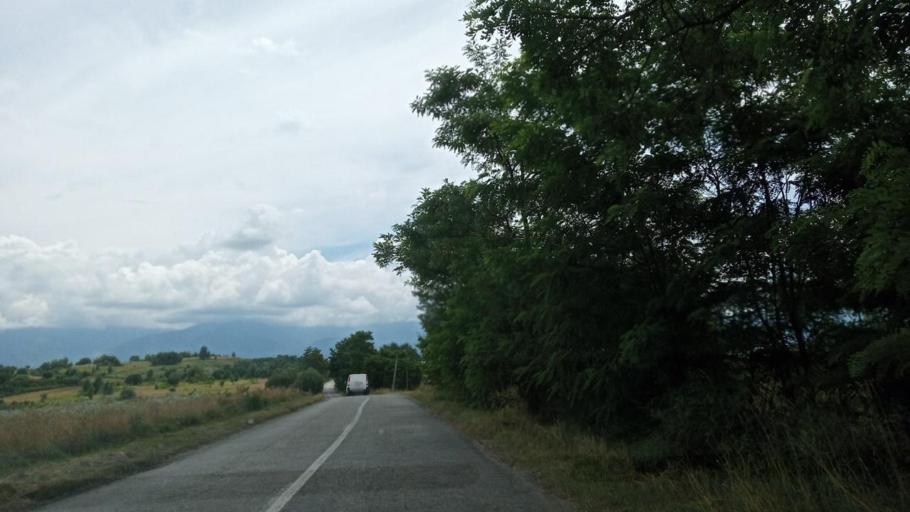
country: RO
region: Sibiu
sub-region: Comuna Porumbacu de Jos
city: Porumbacu de Jos
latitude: 45.7421
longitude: 24.4644
